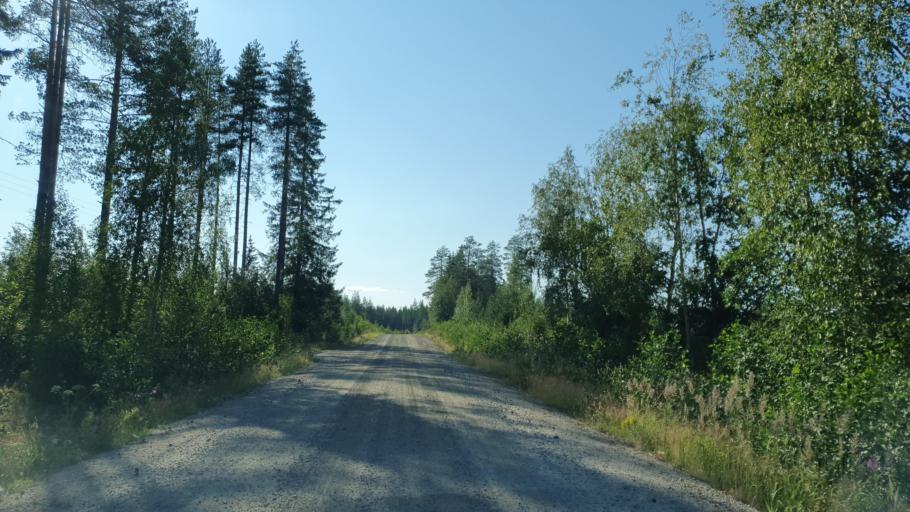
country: FI
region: Kainuu
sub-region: Kehys-Kainuu
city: Kuhmo
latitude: 64.0319
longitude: 29.6872
